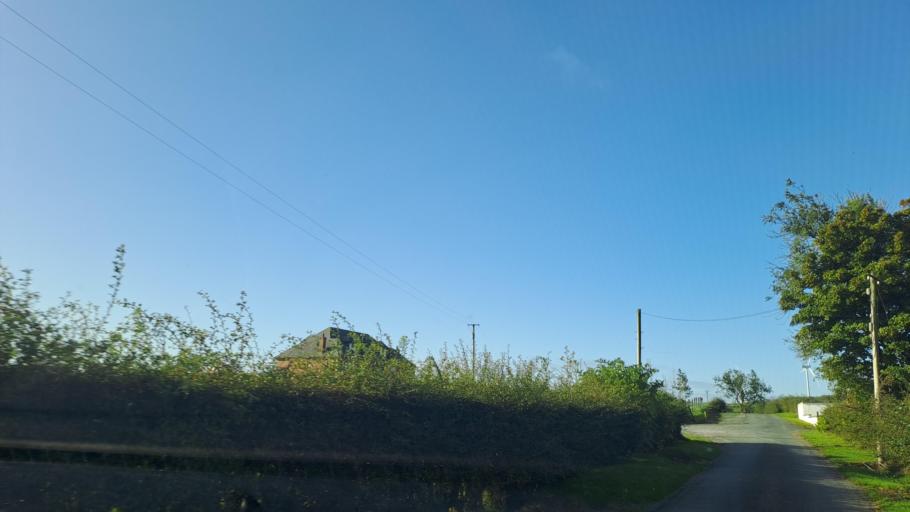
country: IE
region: Ulster
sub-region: An Cabhan
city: Kingscourt
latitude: 53.9586
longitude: -6.8670
